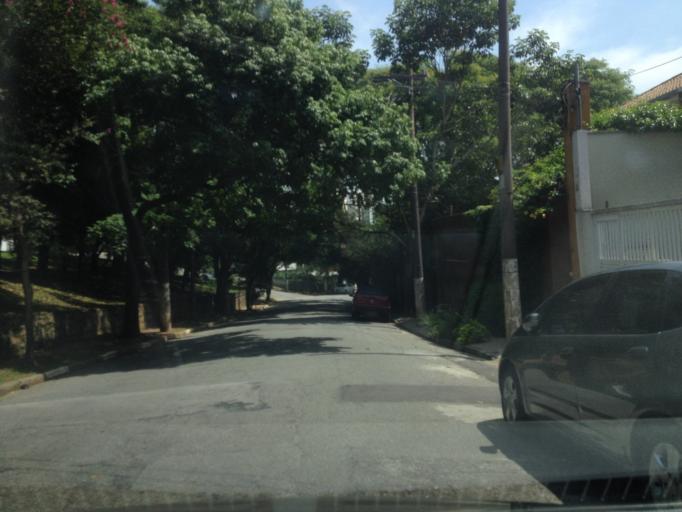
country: BR
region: Sao Paulo
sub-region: Sao Paulo
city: Sao Paulo
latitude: -23.5511
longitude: -46.6873
